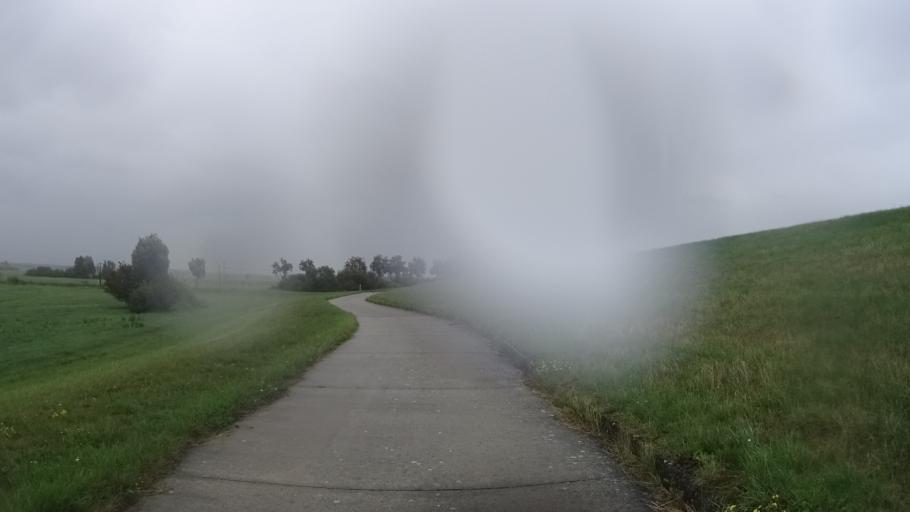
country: DE
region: Lower Saxony
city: Hitzacker
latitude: 53.1616
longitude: 11.0602
